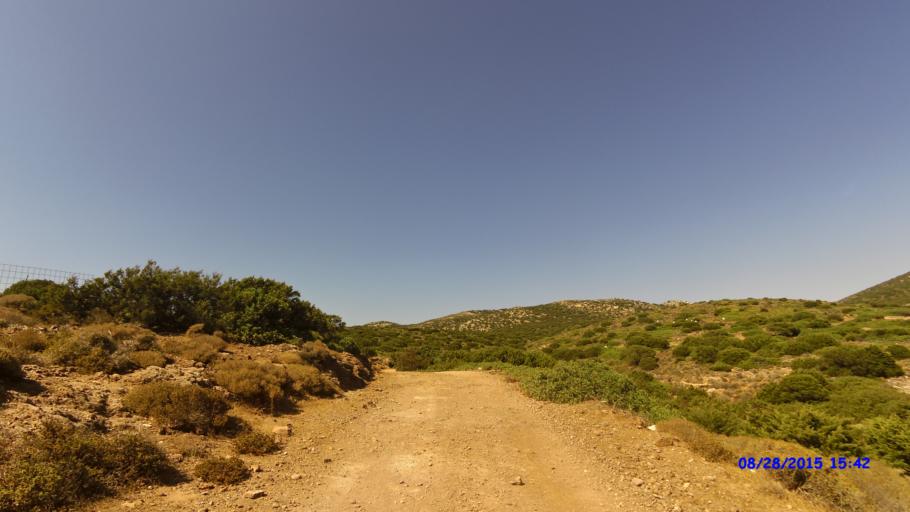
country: GR
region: South Aegean
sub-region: Nomos Kykladon
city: Antiparos
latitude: 36.9900
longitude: 25.0281
